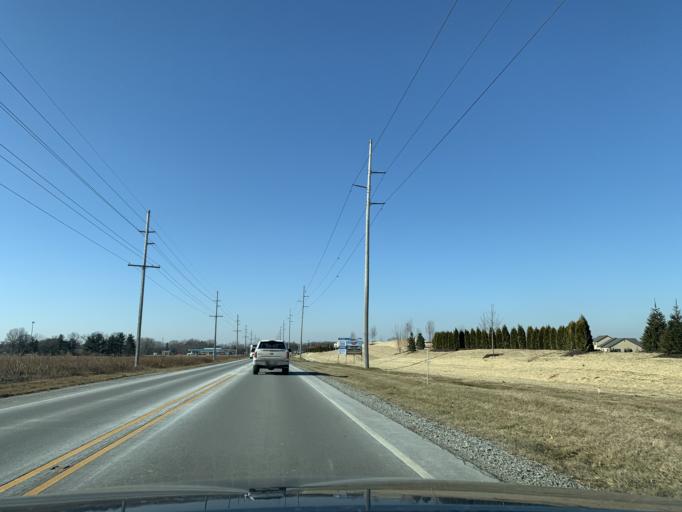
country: US
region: Indiana
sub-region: Lake County
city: Saint John
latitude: 41.4210
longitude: -87.4437
